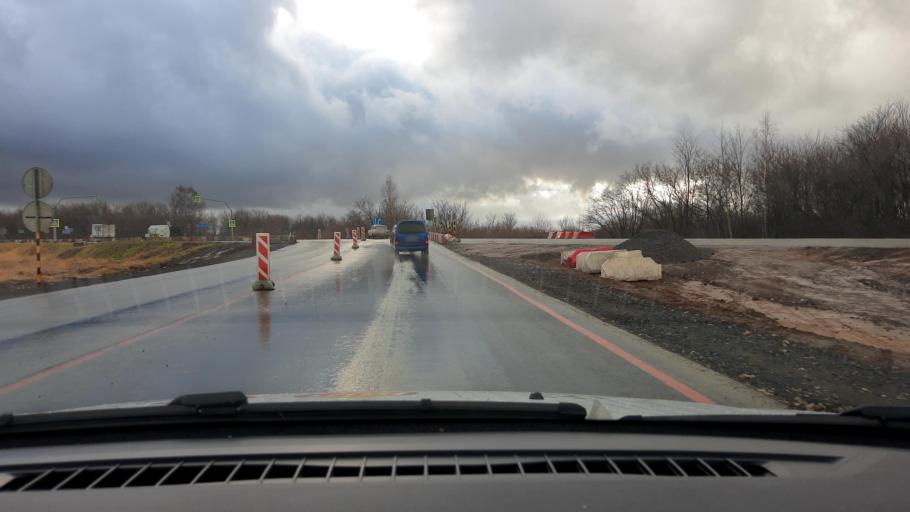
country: RU
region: Nizjnij Novgorod
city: Pamyat' Parizhskoy Kommuny
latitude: 56.0151
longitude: 44.6261
